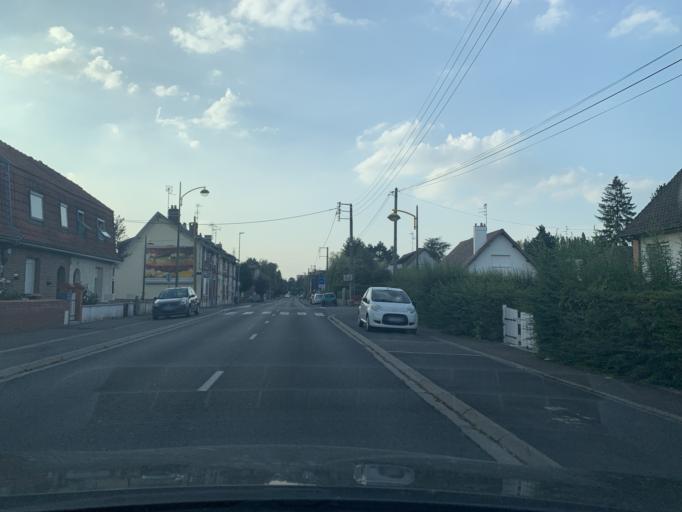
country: FR
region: Nord-Pas-de-Calais
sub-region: Departement du Nord
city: Caudry
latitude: 50.1311
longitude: 3.4035
